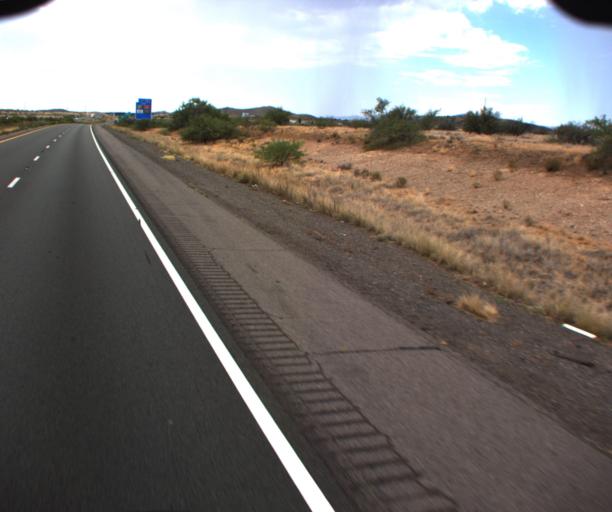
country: US
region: Arizona
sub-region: Yavapai County
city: Cordes Lakes
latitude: 34.3462
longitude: -112.1177
